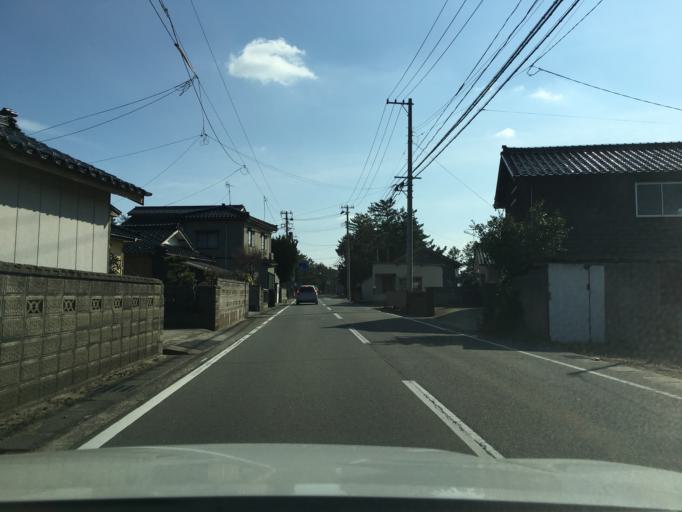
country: JP
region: Yamagata
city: Tsuruoka
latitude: 38.8213
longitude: 139.7786
